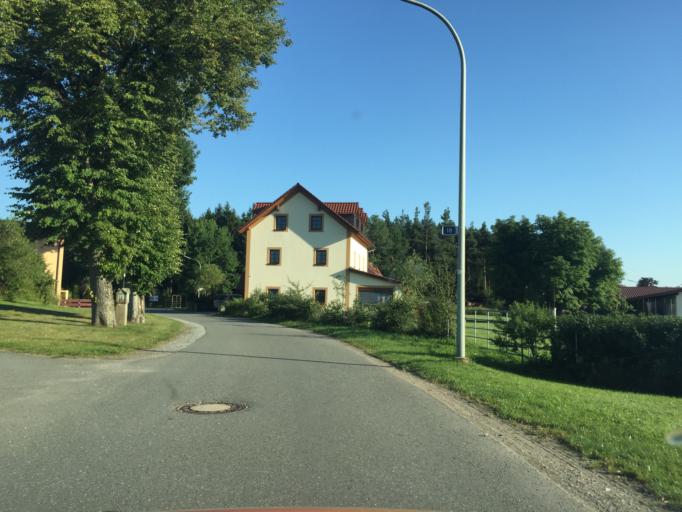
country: DE
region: Bavaria
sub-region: Upper Palatinate
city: Grafenwohr
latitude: 49.7546
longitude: 11.8952
